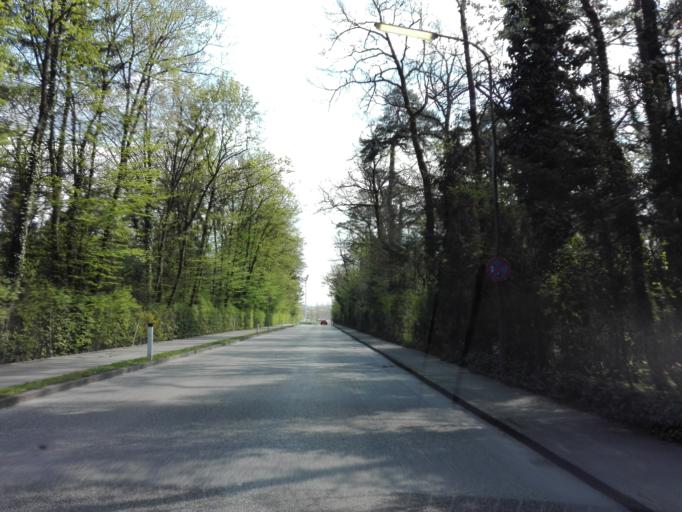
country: AT
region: Upper Austria
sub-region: Politischer Bezirk Linz-Land
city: Traun
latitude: 48.2391
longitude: 14.2524
